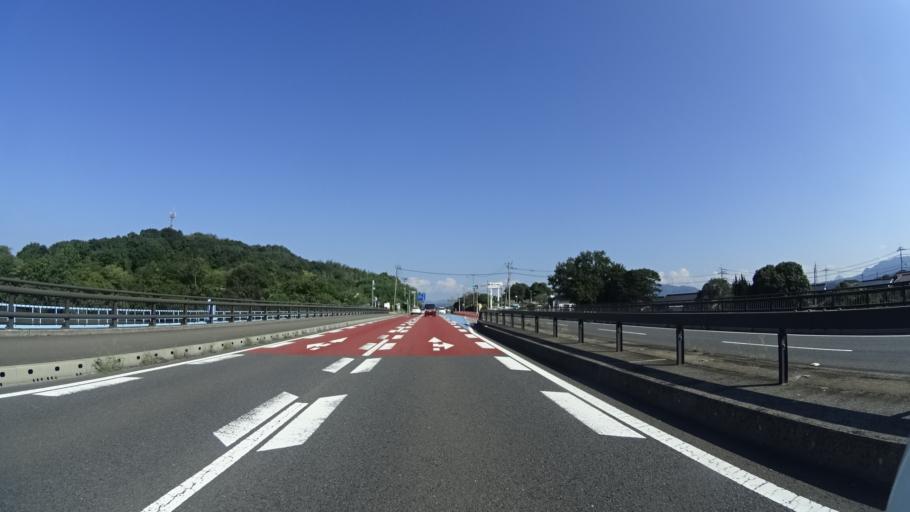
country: JP
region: Fukuoka
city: Yoshitomi
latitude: 33.5881
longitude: 131.1564
